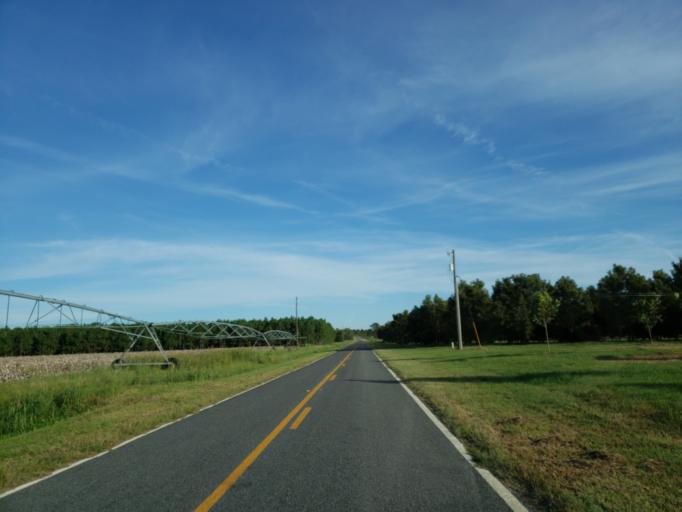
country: US
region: Georgia
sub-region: Dooly County
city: Vienna
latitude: 32.0637
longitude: -83.7713
